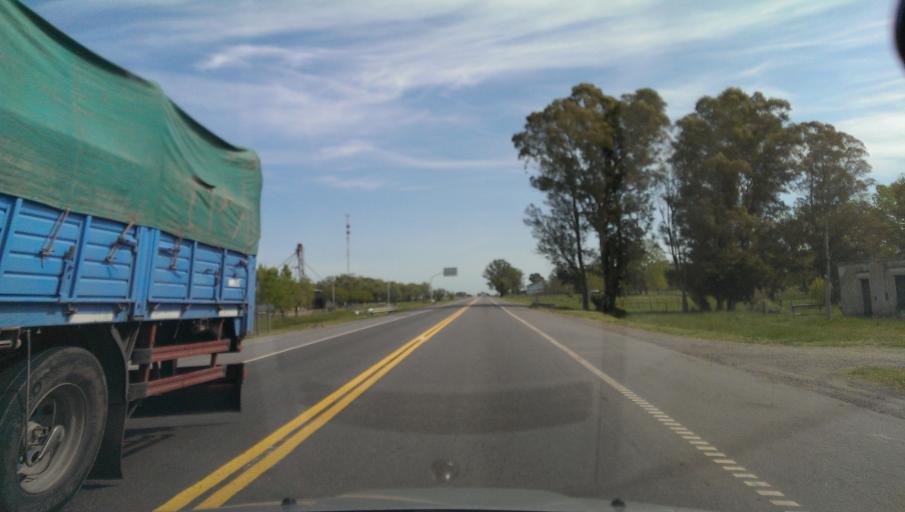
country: AR
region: Buenos Aires
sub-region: Partido de Azul
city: Azul
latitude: -36.3899
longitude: -59.4952
